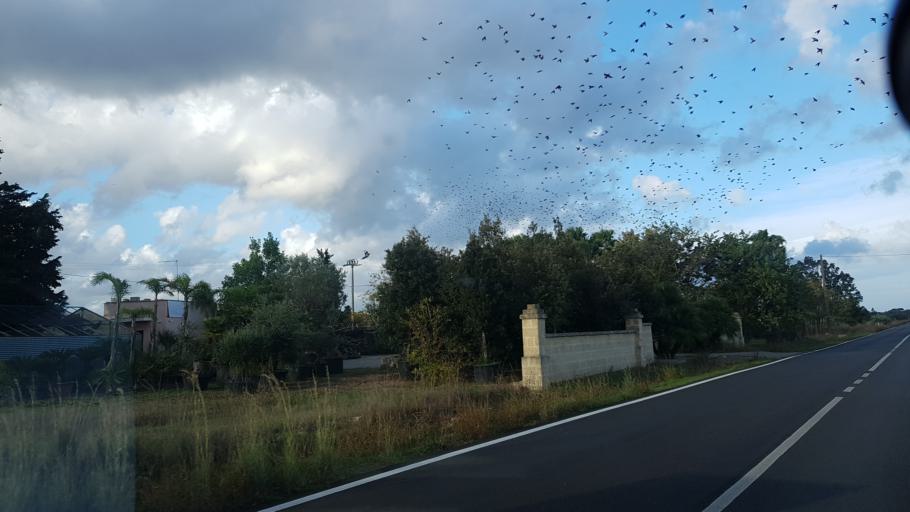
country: IT
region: Apulia
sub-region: Provincia di Brindisi
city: San Pietro Vernotico
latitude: 40.5010
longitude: 18.0050
